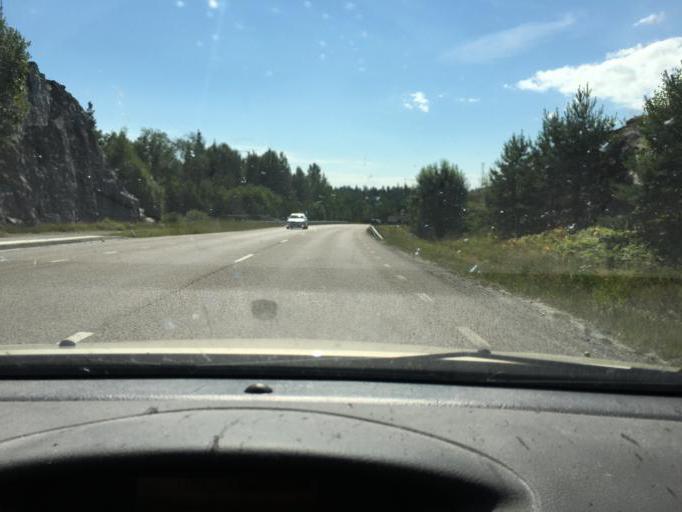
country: SE
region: Stockholm
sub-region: Varmdo Kommun
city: Gustavsberg
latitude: 59.3021
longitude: 18.3895
